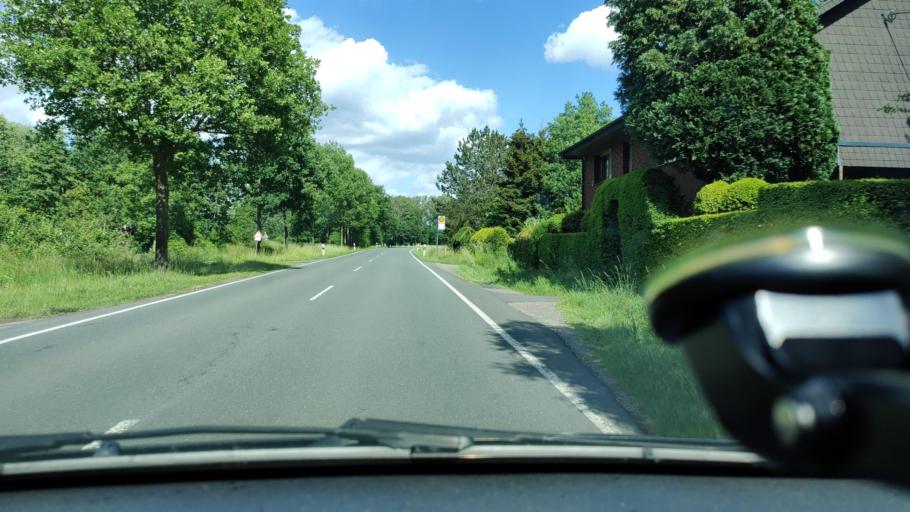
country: DE
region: North Rhine-Westphalia
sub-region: Regierungsbezirk Munster
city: Velen
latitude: 51.8925
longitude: 6.9550
